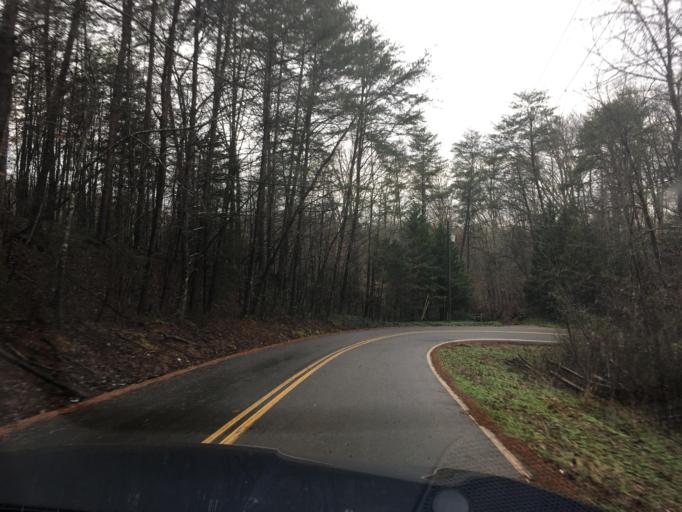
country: US
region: Tennessee
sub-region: McMinn County
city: Englewood
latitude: 35.3630
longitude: -84.4251
